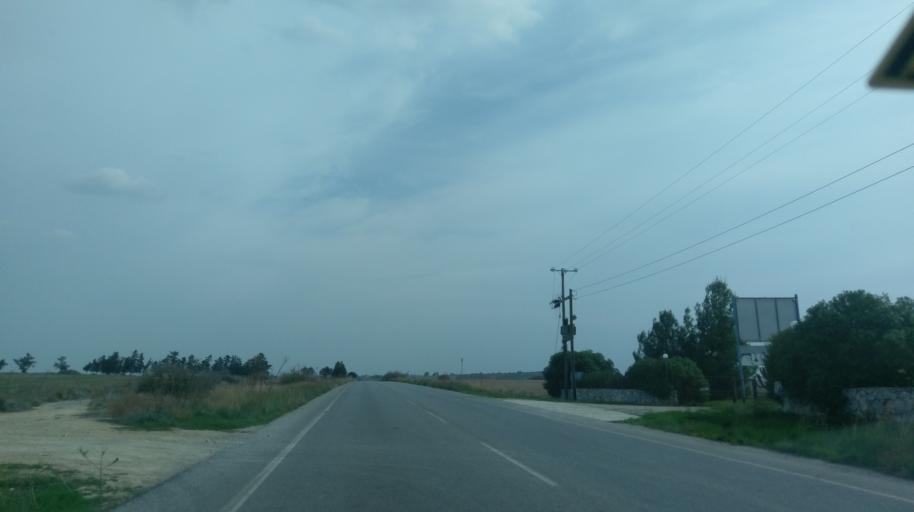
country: CY
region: Ammochostos
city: Lefkonoiko
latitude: 35.2620
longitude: 33.7550
